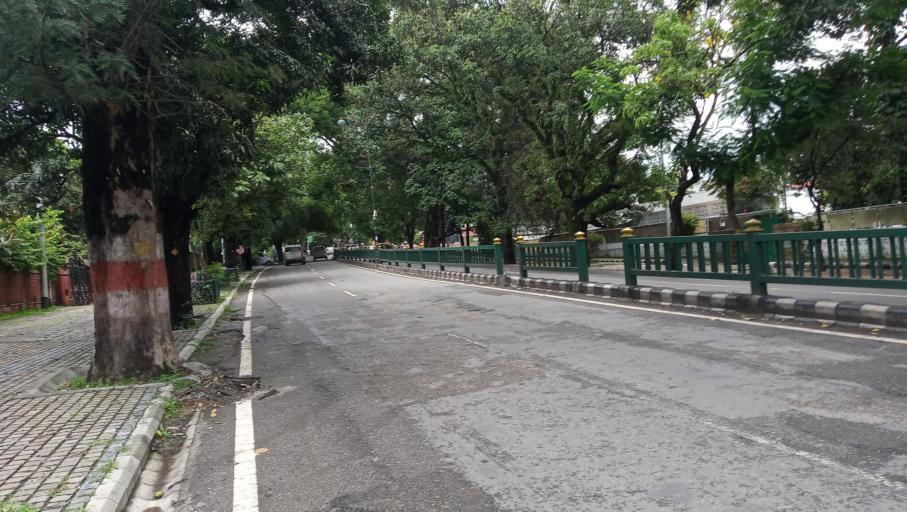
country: IN
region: Uttarakhand
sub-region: Dehradun
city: Dehradun
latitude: 30.3673
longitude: 78.0721
